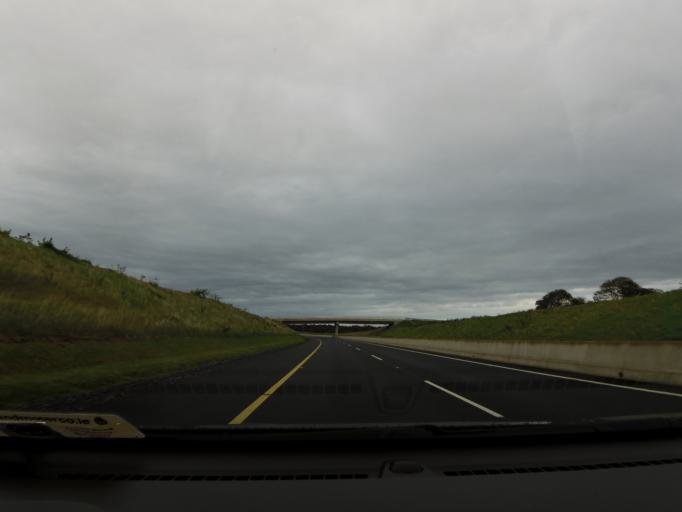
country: IE
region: Connaught
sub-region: County Galway
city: Athenry
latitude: 53.3592
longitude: -8.7900
